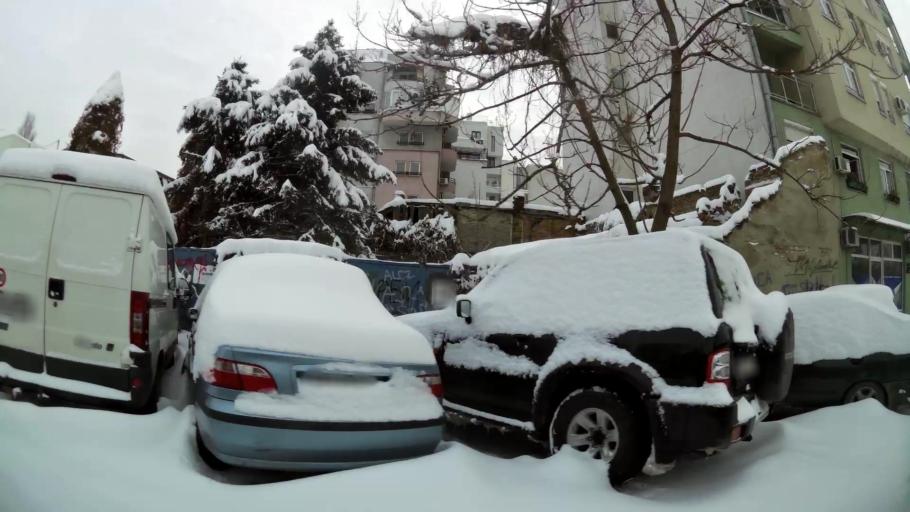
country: RS
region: Central Serbia
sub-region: Belgrade
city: Stari Grad
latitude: 44.8219
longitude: 20.4719
